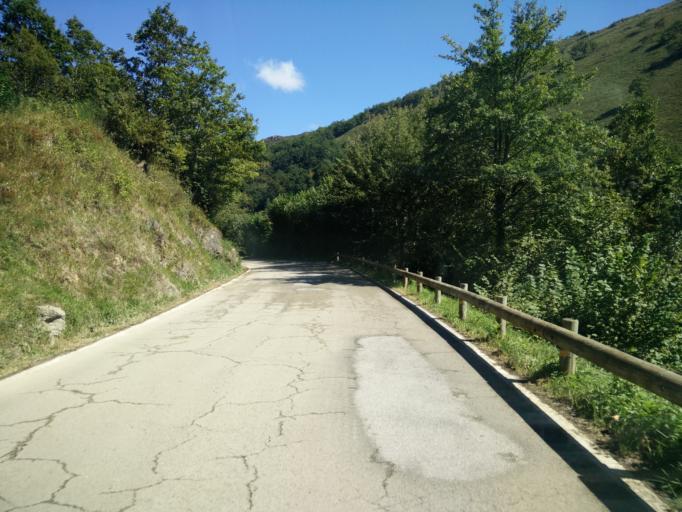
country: ES
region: Cantabria
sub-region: Provincia de Cantabria
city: Ruente
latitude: 43.1501
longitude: -4.2835
